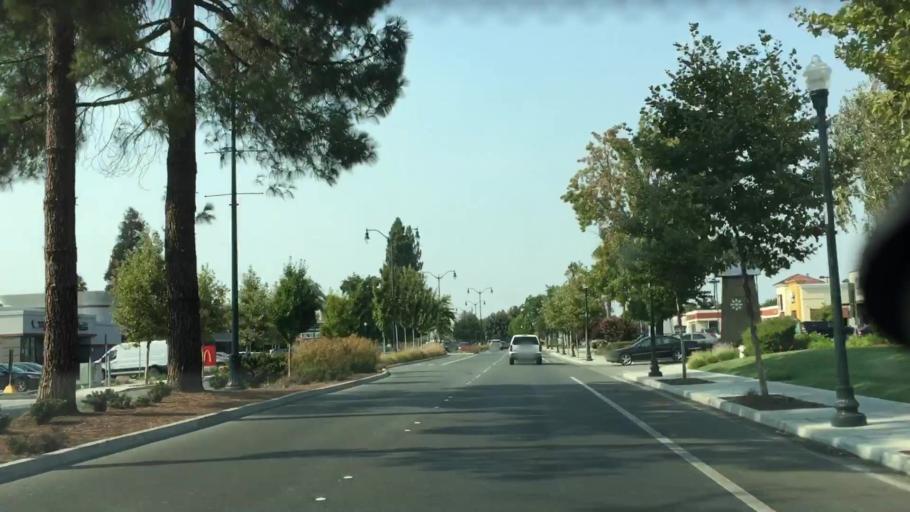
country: US
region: California
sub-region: Contra Costa County
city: Pacheco
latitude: 37.9729
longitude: -122.0639
